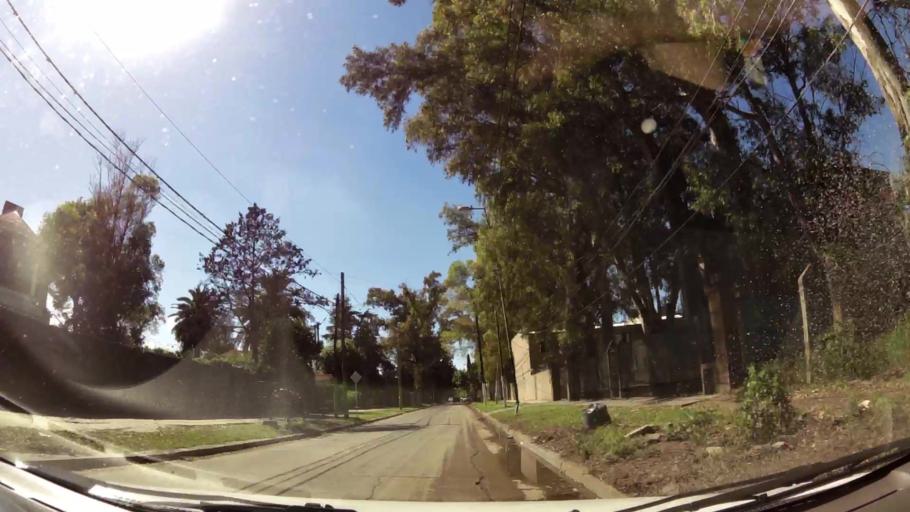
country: AR
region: Buenos Aires
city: Ituzaingo
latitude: -34.6249
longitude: -58.6603
